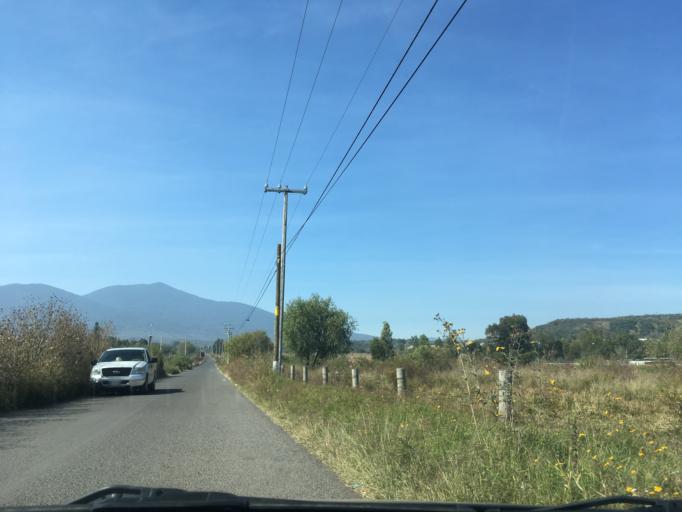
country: MX
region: Michoacan
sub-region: Morelia
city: La Mintzita (Piedra Dura)
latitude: 19.6507
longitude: -101.2824
